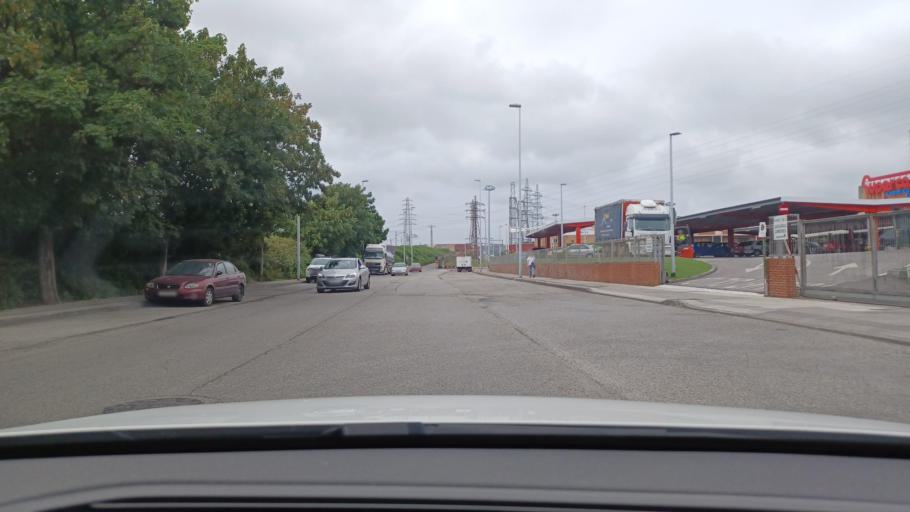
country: ES
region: Asturias
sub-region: Province of Asturias
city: Aviles
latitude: 43.5718
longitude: -5.9260
